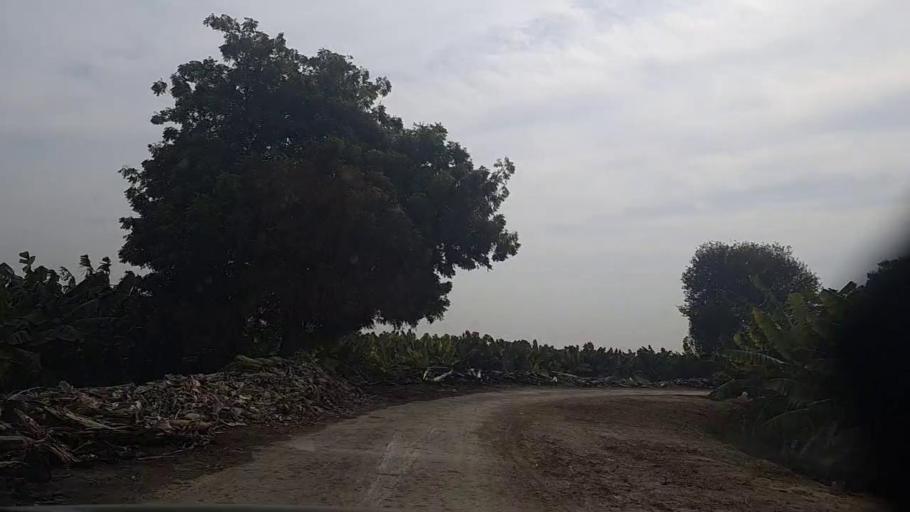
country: PK
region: Sindh
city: Sakrand
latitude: 26.2401
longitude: 68.2971
